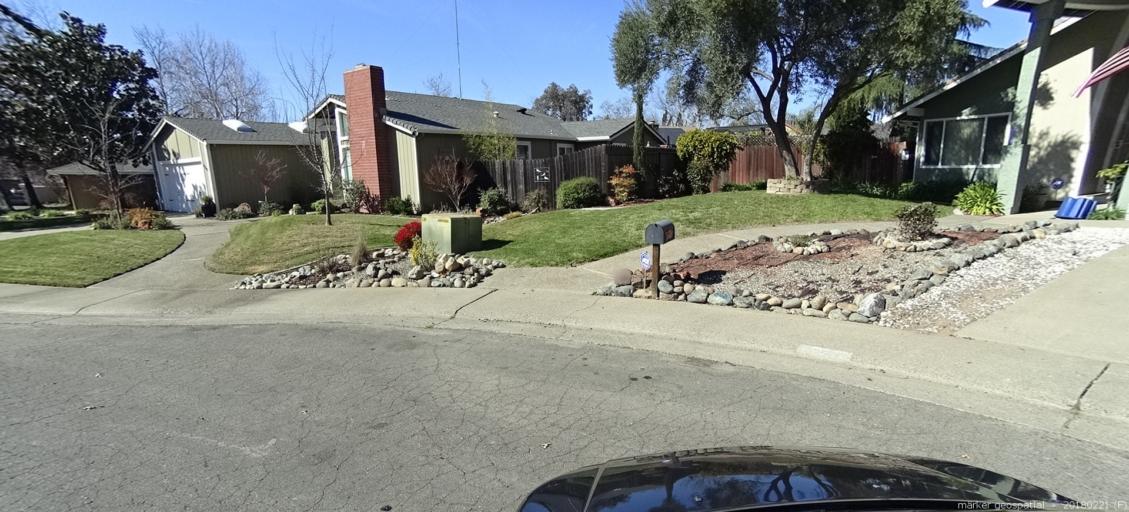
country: US
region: California
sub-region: Sacramento County
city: Orangevale
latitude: 38.6794
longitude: -121.2541
